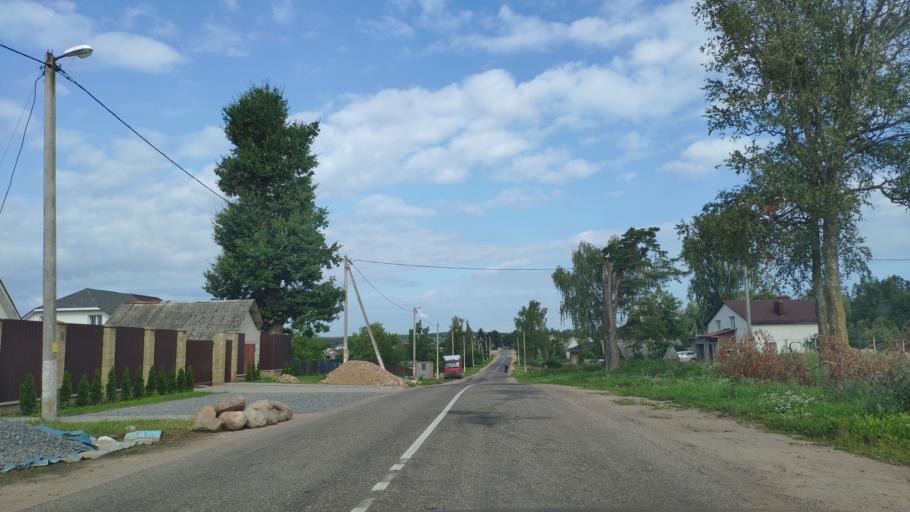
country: BY
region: Minsk
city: Khatsyezhyna
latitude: 53.8872
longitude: 27.2666
